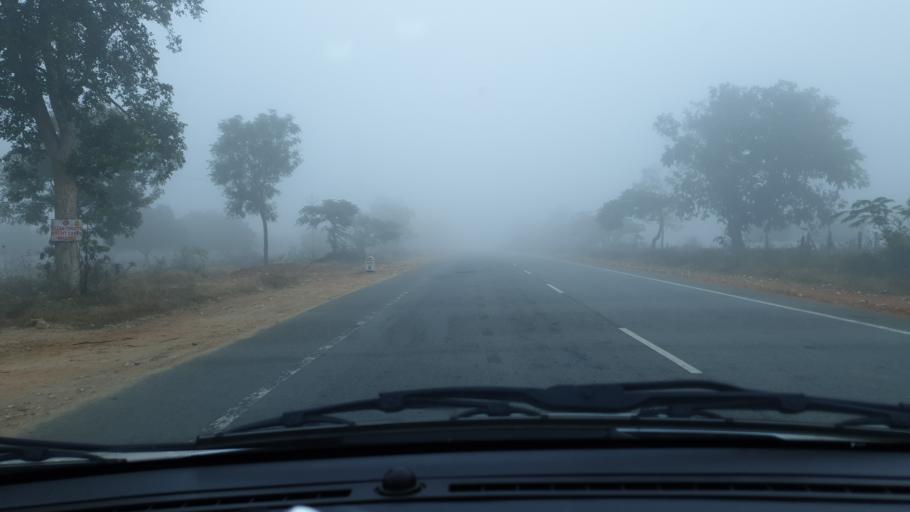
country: IN
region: Telangana
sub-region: Mahbubnagar
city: Nagar Karnul
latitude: 16.6474
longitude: 78.5815
